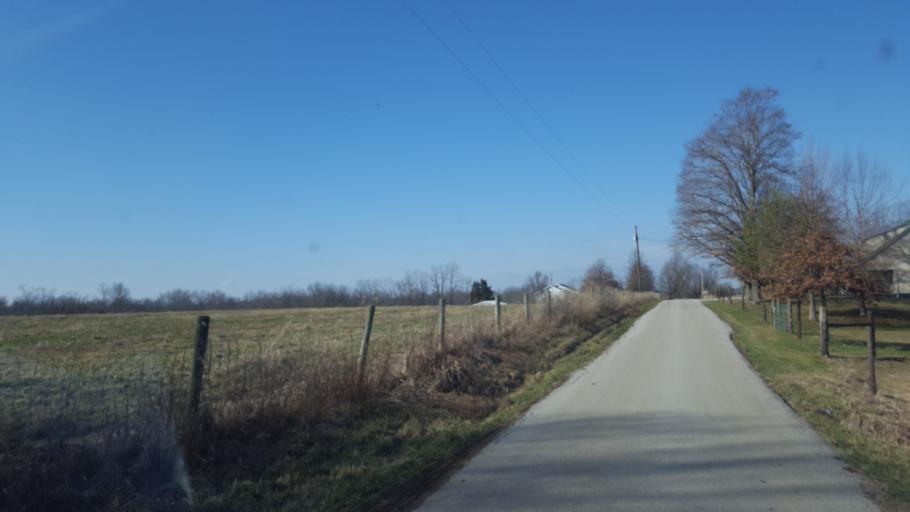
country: US
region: Kentucky
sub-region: Henry County
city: Eminence
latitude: 38.2981
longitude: -85.0342
